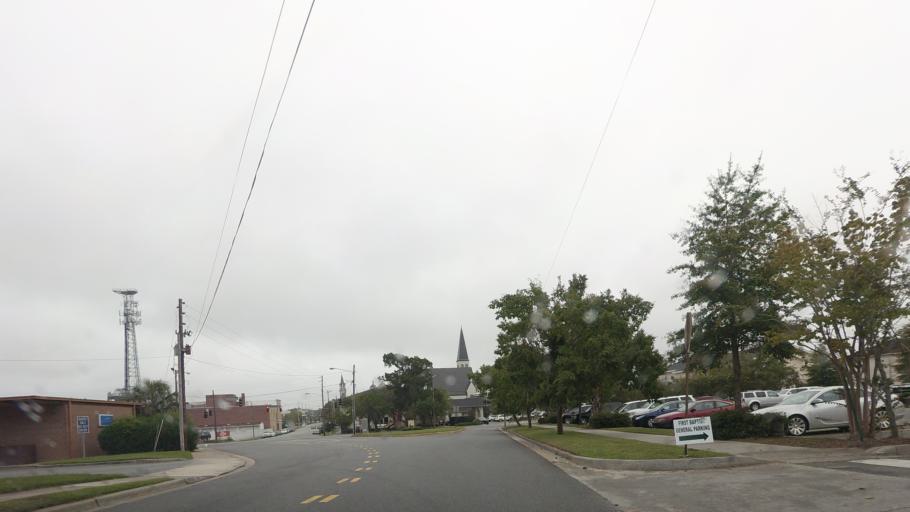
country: US
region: Georgia
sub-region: Lowndes County
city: Valdosta
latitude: 30.8313
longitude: -83.2833
